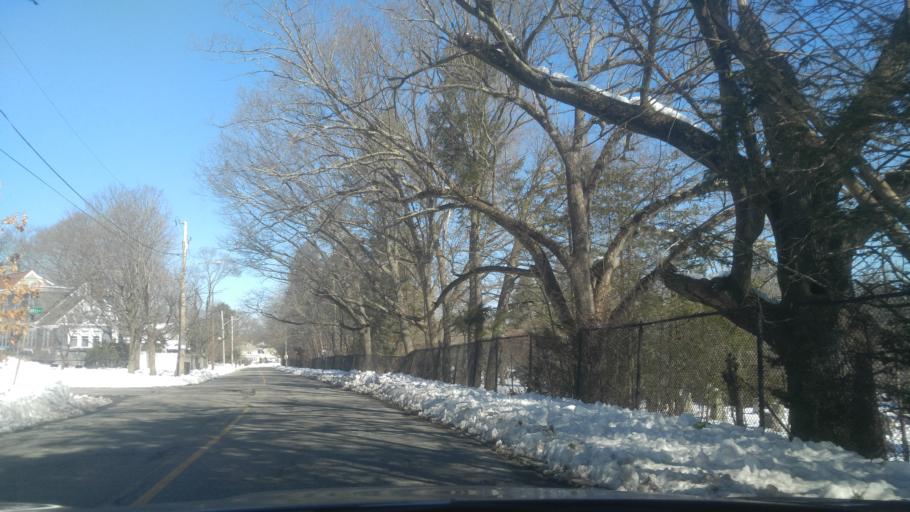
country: US
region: Rhode Island
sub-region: Providence County
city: Pawtucket
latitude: 41.8596
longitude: -71.3837
